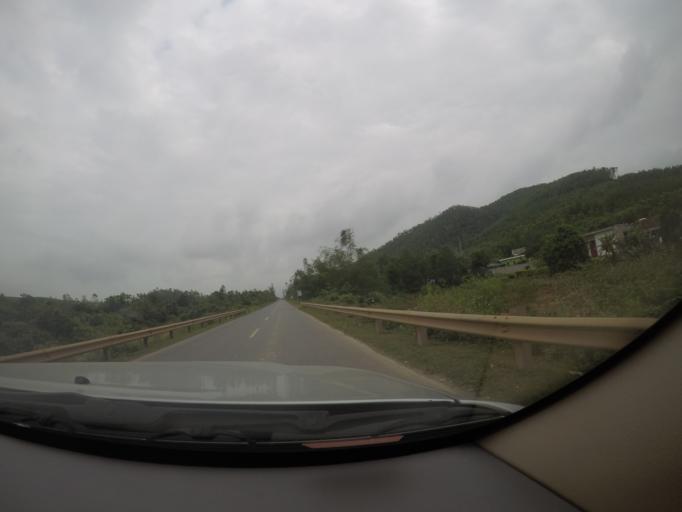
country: VN
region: Quang Binh
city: Quan Hau
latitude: 17.2747
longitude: 106.6561
